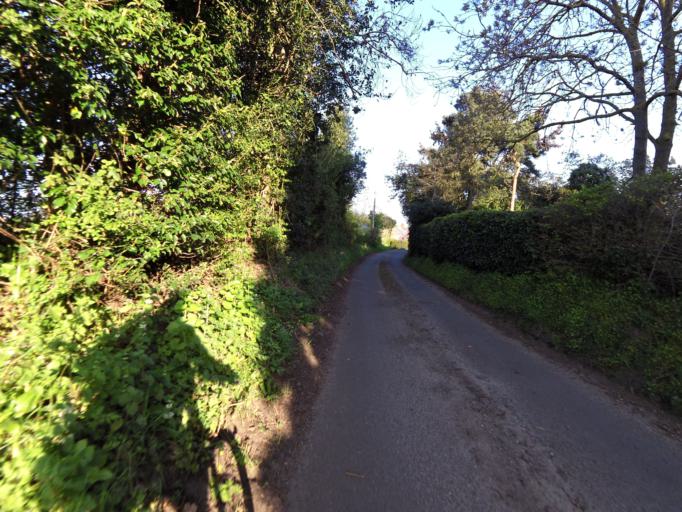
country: GB
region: England
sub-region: Suffolk
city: Bramford
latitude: 52.0458
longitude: 1.0649
